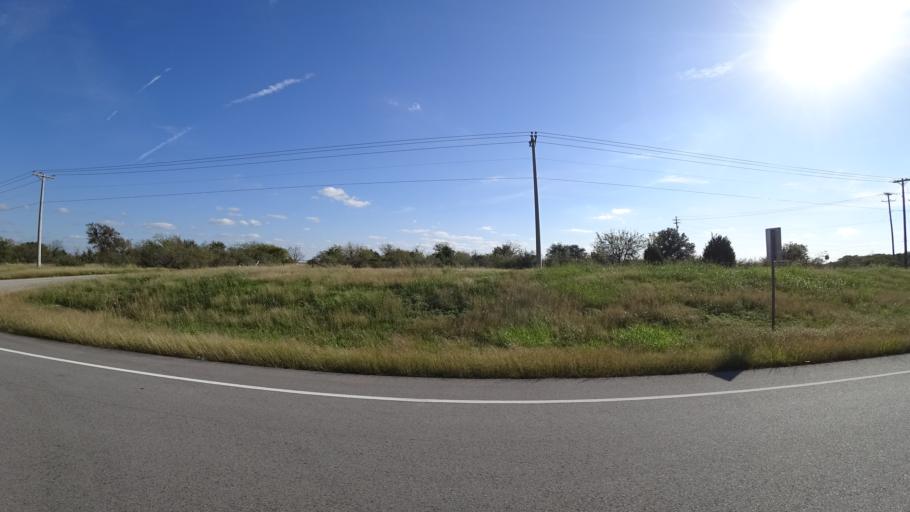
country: US
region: Texas
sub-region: Travis County
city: Wells Branch
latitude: 30.4607
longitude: -97.6976
